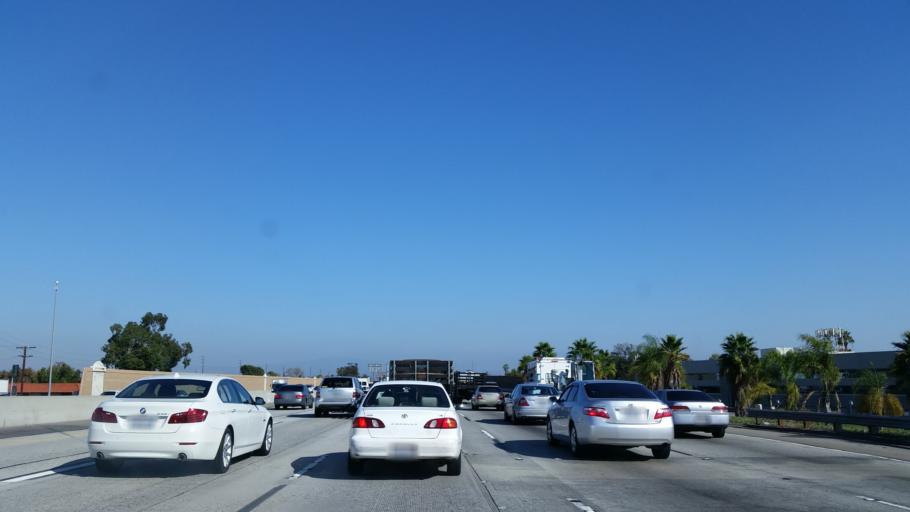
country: US
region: California
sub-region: Orange County
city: Garden Grove
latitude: 33.7659
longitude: -117.9376
